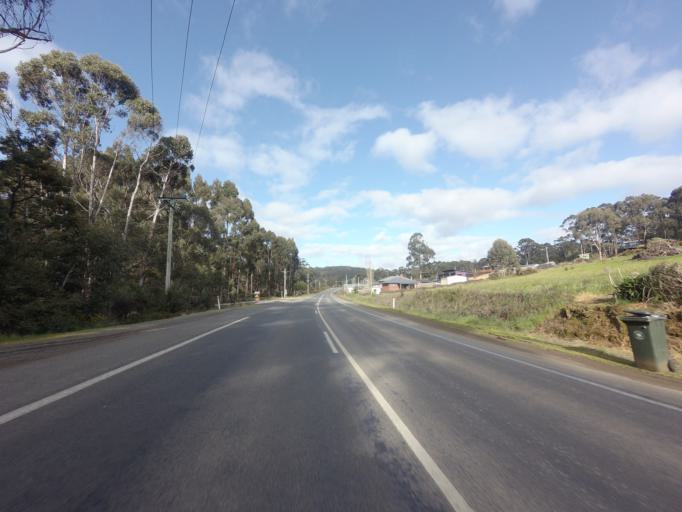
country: AU
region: Tasmania
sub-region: Huon Valley
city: Geeveston
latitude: -43.1631
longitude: 146.9493
